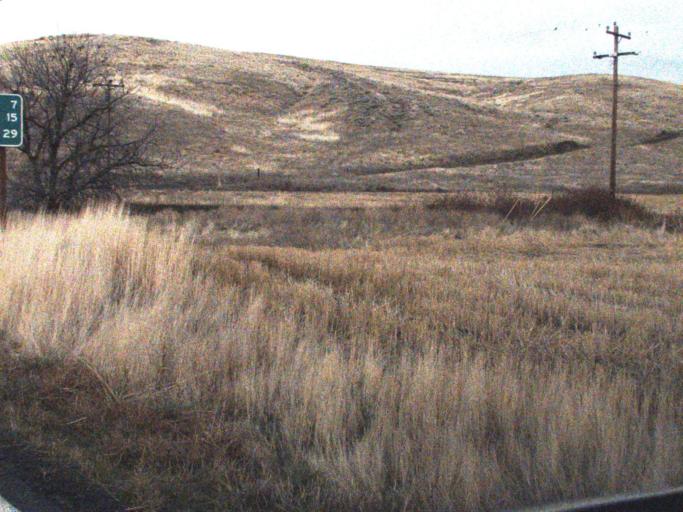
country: US
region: Washington
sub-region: Columbia County
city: Dayton
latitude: 46.5116
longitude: -117.9729
